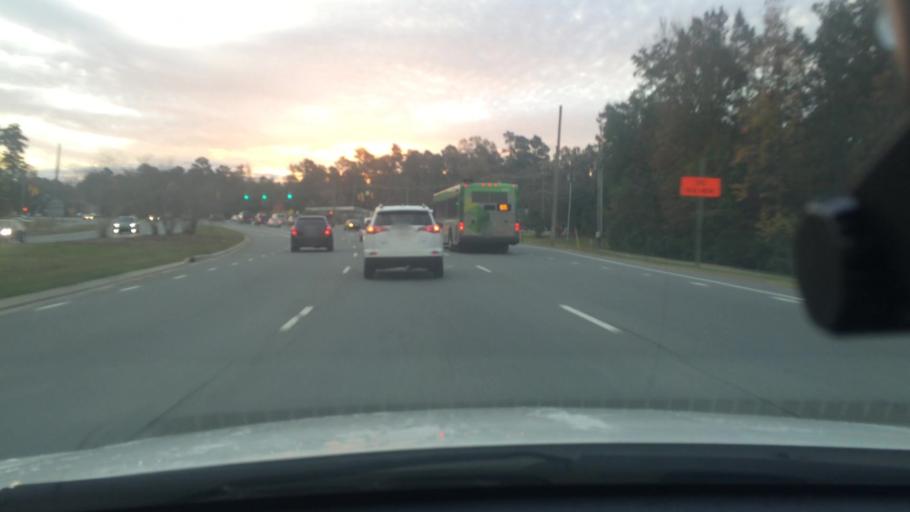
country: US
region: North Carolina
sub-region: Orange County
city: Chapel Hill
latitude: 35.9019
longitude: -79.0094
